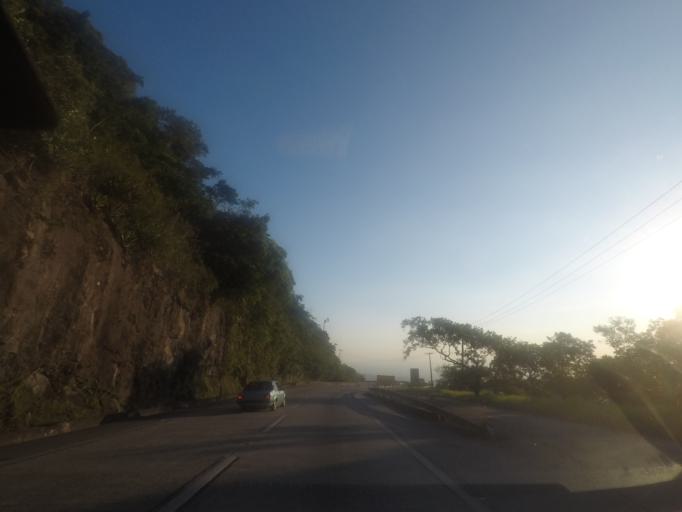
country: BR
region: Rio de Janeiro
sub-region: Petropolis
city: Petropolis
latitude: -22.5287
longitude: -43.2350
